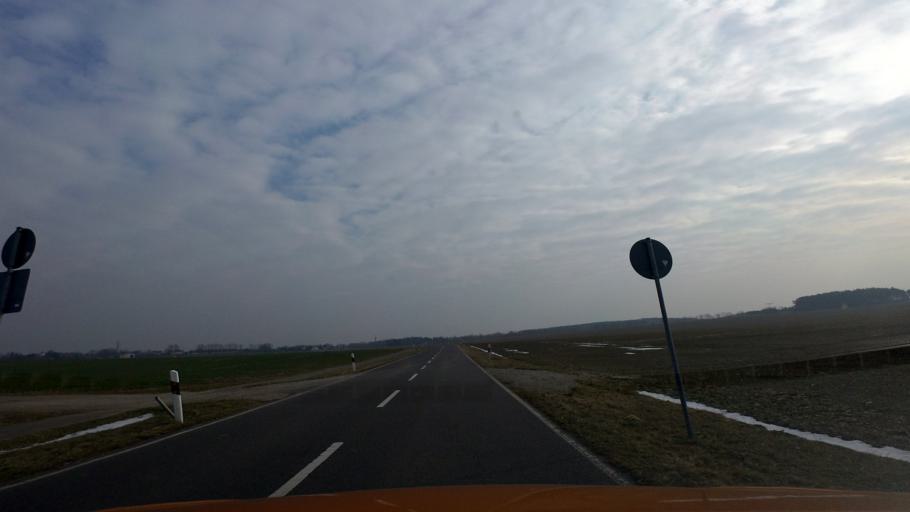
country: DE
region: Brandenburg
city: Rangsdorf
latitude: 52.2461
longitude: 13.3652
